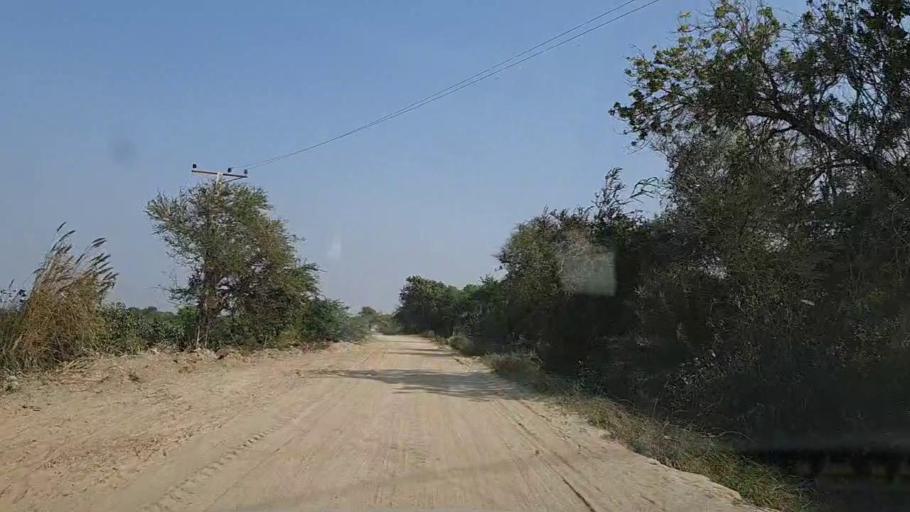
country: PK
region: Sindh
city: Mirpur Sakro
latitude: 24.5580
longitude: 67.5972
